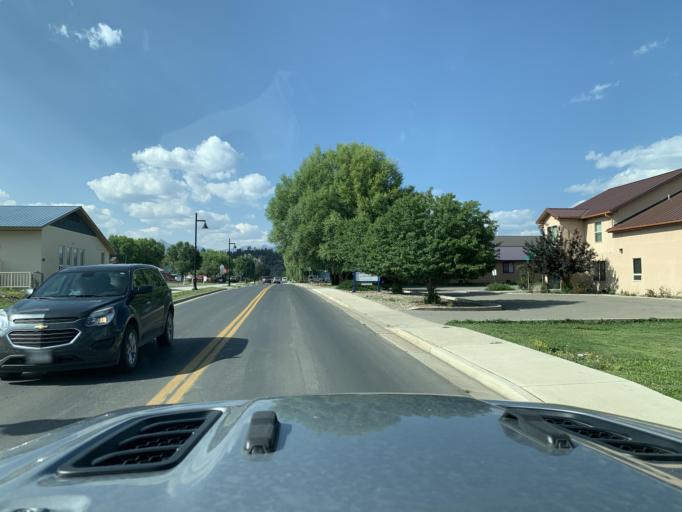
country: US
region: Colorado
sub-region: Archuleta County
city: Pagosa Springs
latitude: 37.2599
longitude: -107.0172
